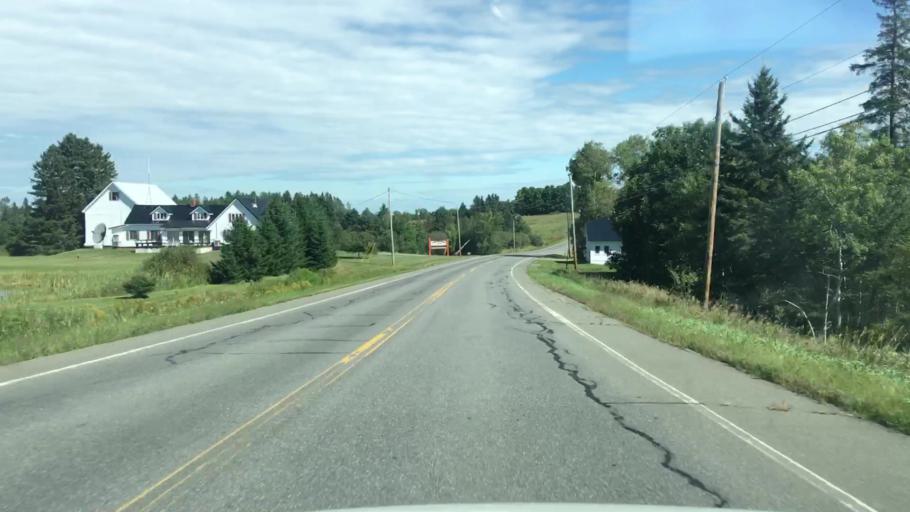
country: US
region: Maine
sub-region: Penobscot County
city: Dexter
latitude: 45.0711
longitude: -69.2375
